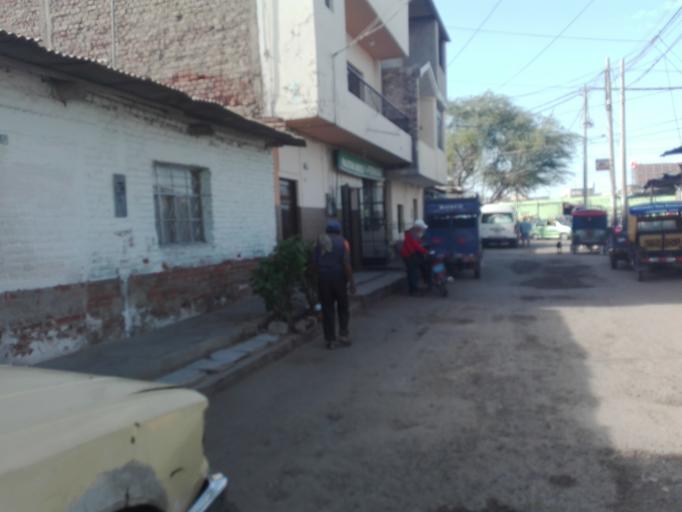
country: PE
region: Piura
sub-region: Provincia de Piura
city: Piura
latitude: -5.1859
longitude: -80.6330
